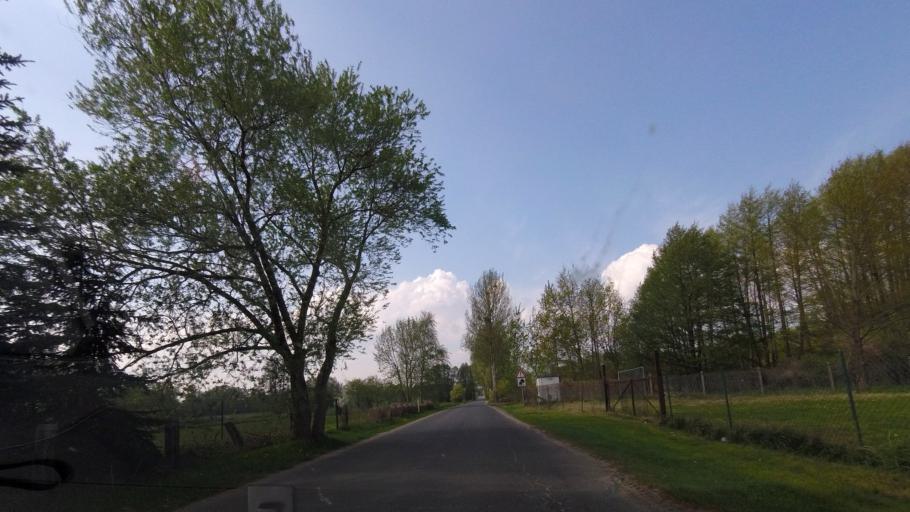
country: DE
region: Saxony-Anhalt
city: Zahna
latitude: 51.9137
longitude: 12.7959
